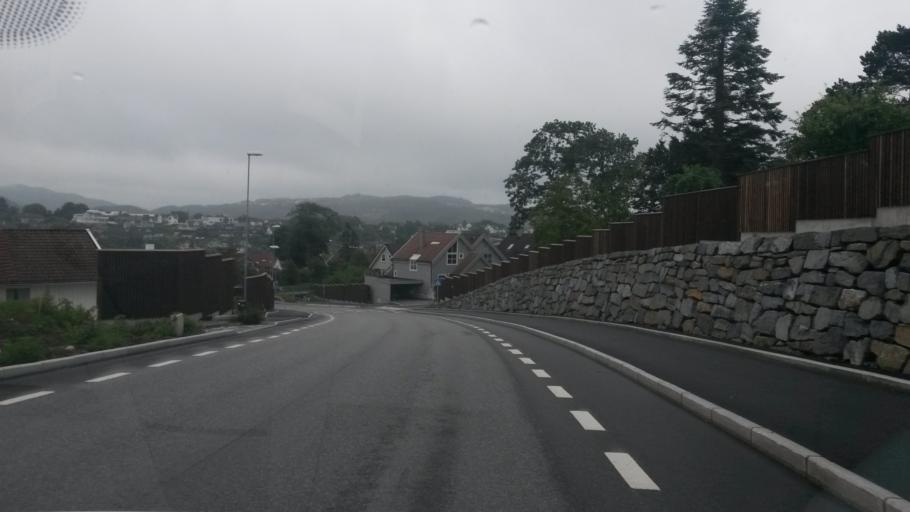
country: NO
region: Rogaland
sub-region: Sandnes
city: Sandnes
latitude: 58.8307
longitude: 5.7148
